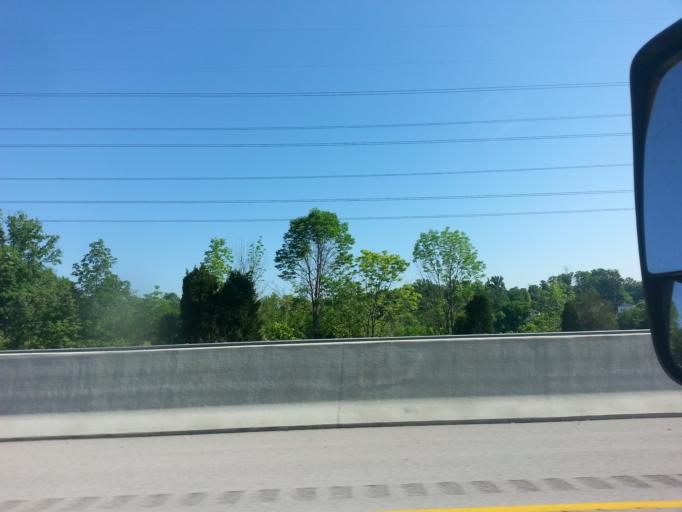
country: US
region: Kentucky
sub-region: Jefferson County
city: Middletown
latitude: 38.2220
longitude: -85.4863
